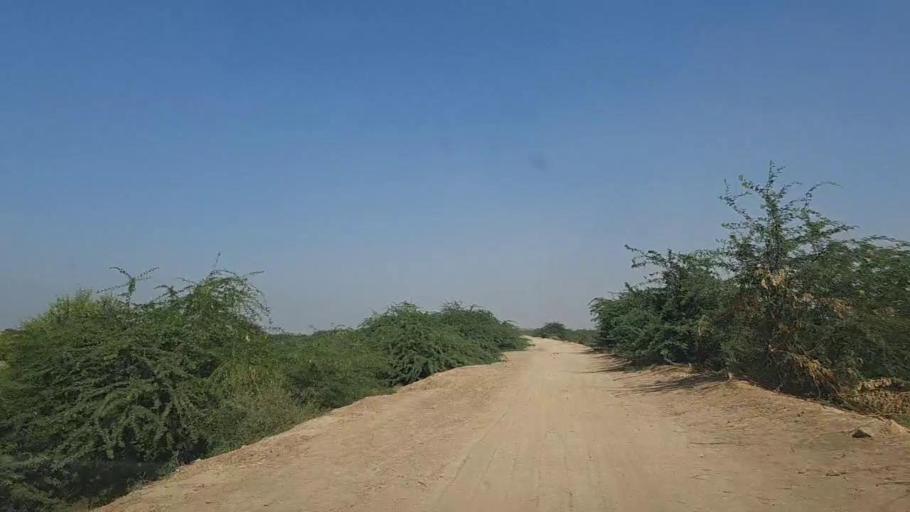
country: PK
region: Sindh
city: Daro Mehar
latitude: 24.8803
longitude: 68.0552
